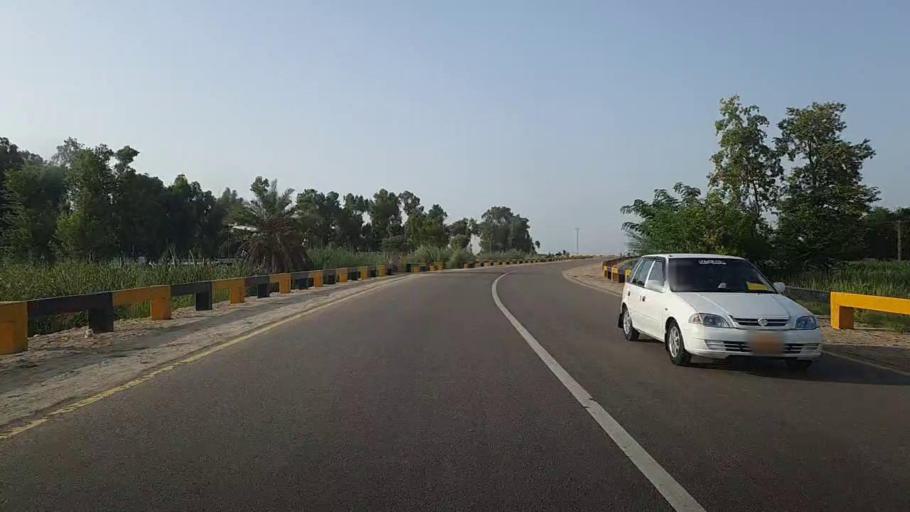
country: PK
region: Sindh
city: Naushahro Firoz
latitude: 26.7904
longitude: 68.1442
